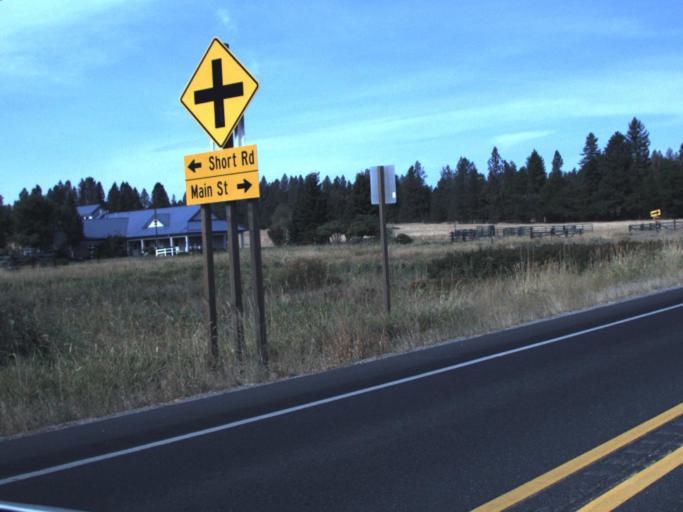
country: US
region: Washington
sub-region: Spokane County
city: Deer Park
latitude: 47.9421
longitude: -117.4768
